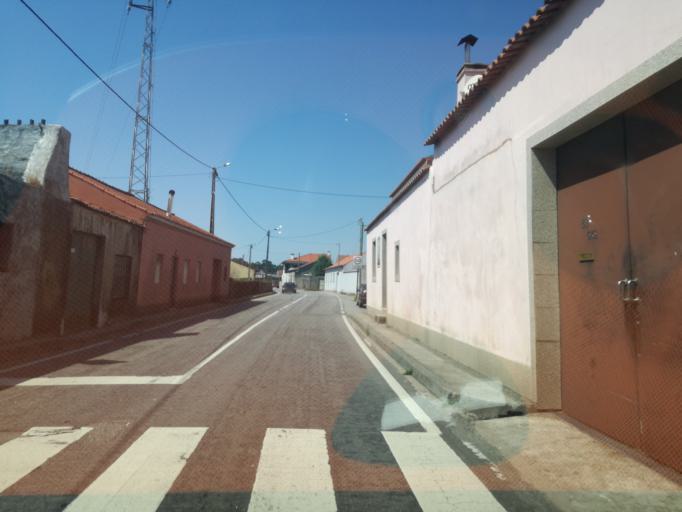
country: PT
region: Braga
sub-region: Esposende
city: Apulia
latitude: 41.4924
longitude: -8.7548
